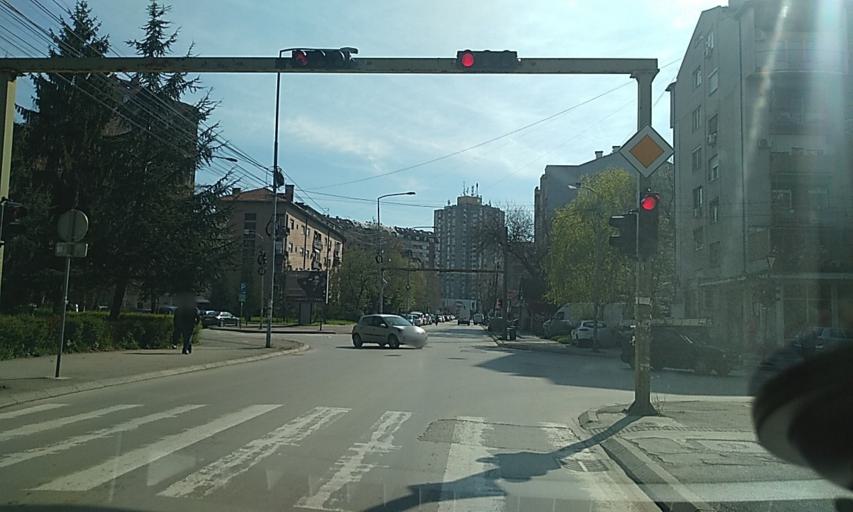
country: RS
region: Central Serbia
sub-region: Nisavski Okrug
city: Nis
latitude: 43.3182
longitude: 21.9046
